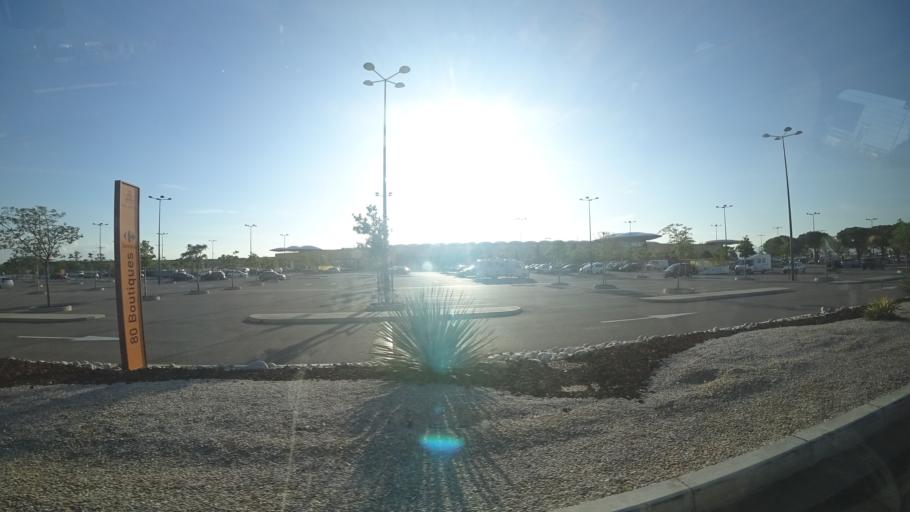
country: FR
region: Languedoc-Roussillon
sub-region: Departement des Pyrenees-Orientales
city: Pia
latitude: 42.7751
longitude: 2.9157
